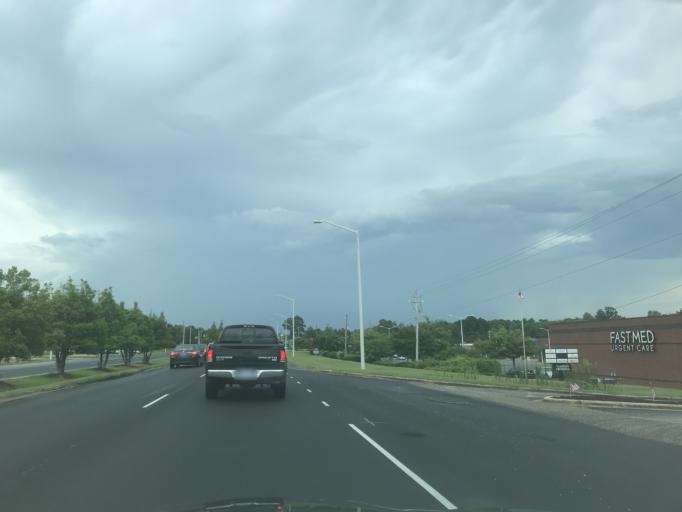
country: US
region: North Carolina
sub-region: Johnston County
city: Clayton
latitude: 35.6524
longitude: -78.4720
